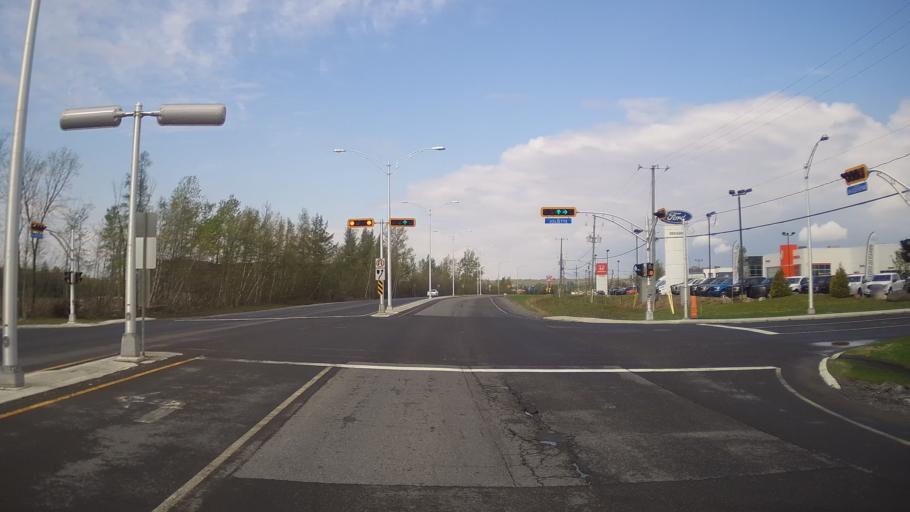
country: CA
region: Quebec
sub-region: Monteregie
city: Cowansville
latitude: 45.1895
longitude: -72.7480
